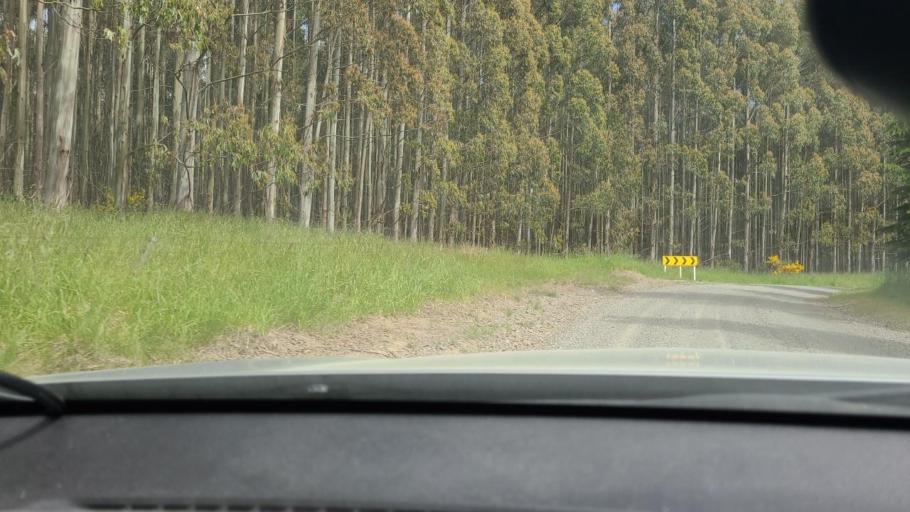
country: NZ
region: Southland
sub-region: Southland District
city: Riverton
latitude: -45.9066
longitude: 167.9436
